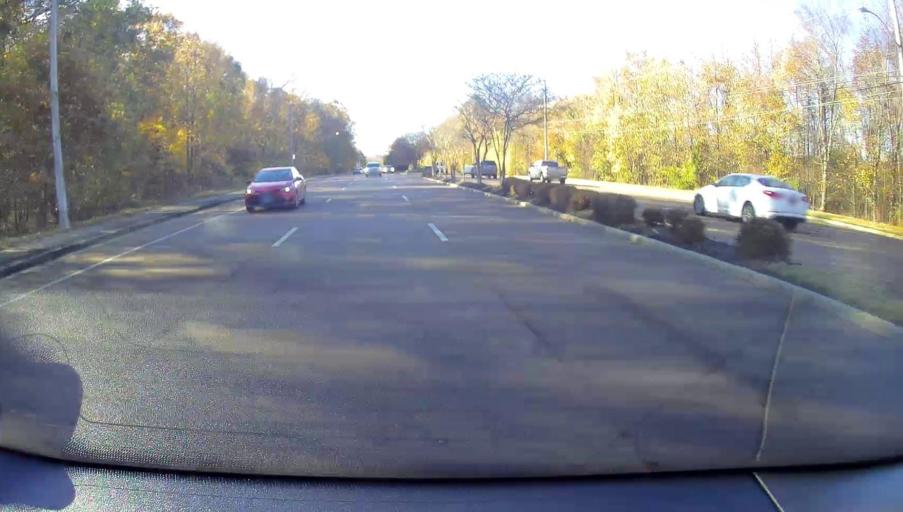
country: US
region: Tennessee
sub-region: Shelby County
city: Germantown
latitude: 35.1152
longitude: -89.8160
